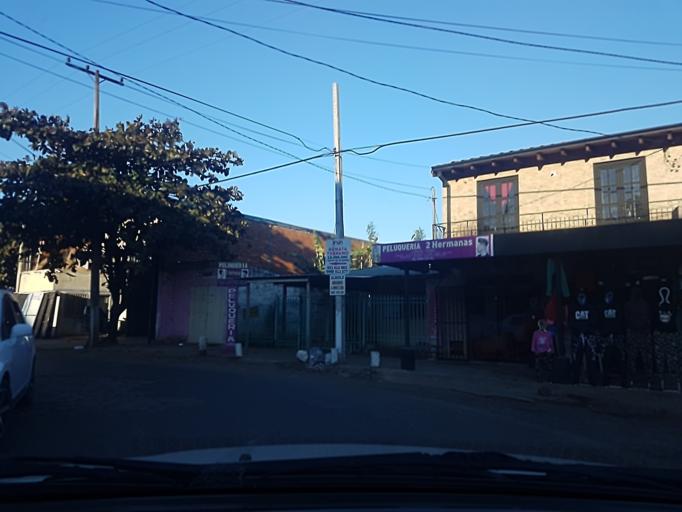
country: PY
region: Central
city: Colonia Mariano Roque Alonso
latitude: -25.2169
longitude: -57.5233
